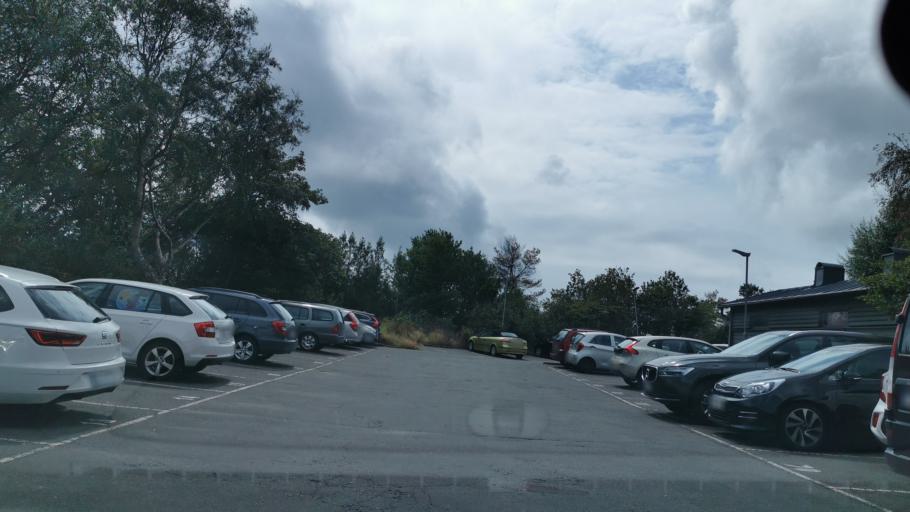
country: SE
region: Vaestra Goetaland
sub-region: Goteborg
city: Goeteborg
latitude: 57.6777
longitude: 11.9762
